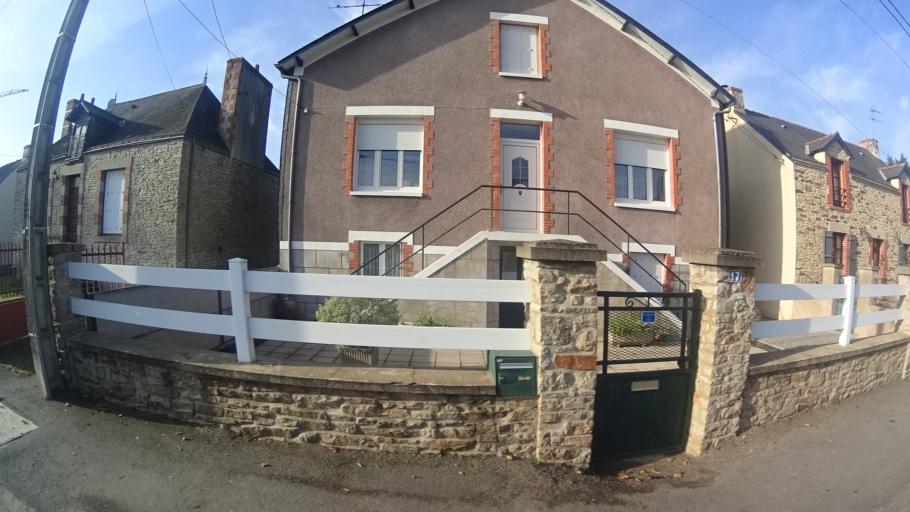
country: FR
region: Brittany
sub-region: Departement du Morbihan
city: Allaire
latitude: 47.6342
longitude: -2.1643
